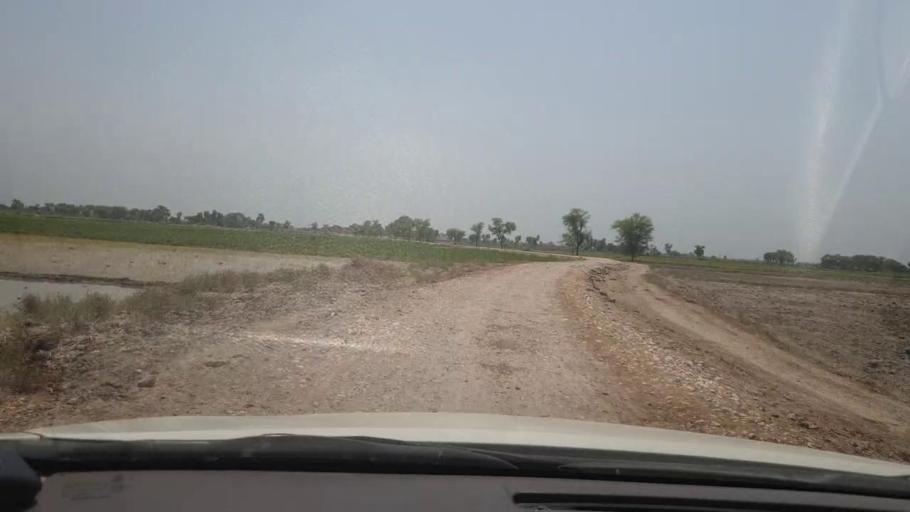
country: PK
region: Sindh
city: Garhi Yasin
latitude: 27.9162
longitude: 68.5563
